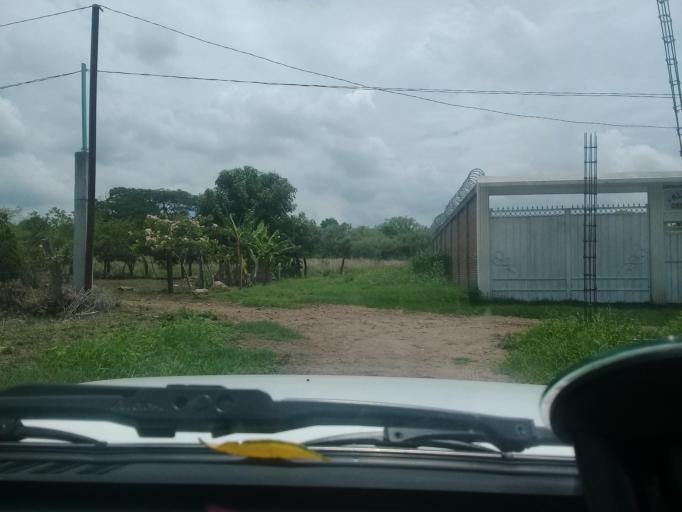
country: MX
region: Veracruz
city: Paso de Ovejas
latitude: 19.2942
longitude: -96.4408
